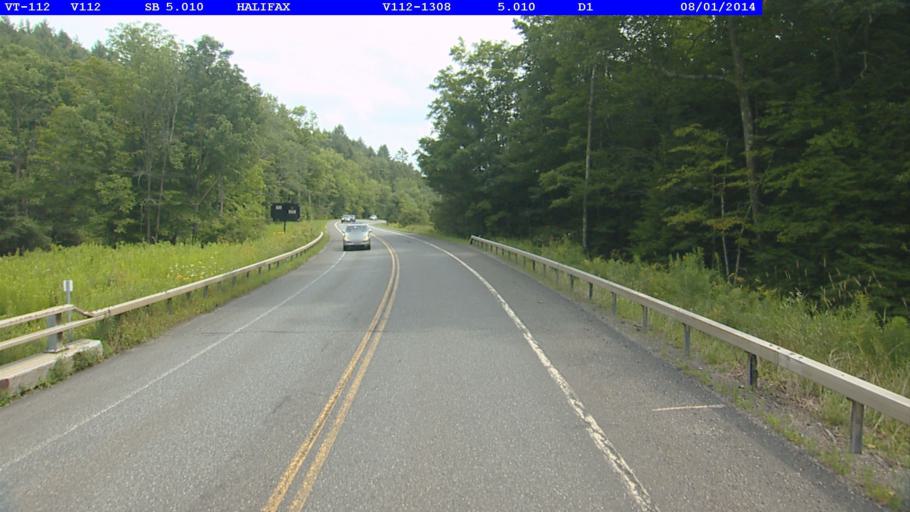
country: US
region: Massachusetts
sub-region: Franklin County
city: Colrain
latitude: 42.7684
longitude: -72.7979
